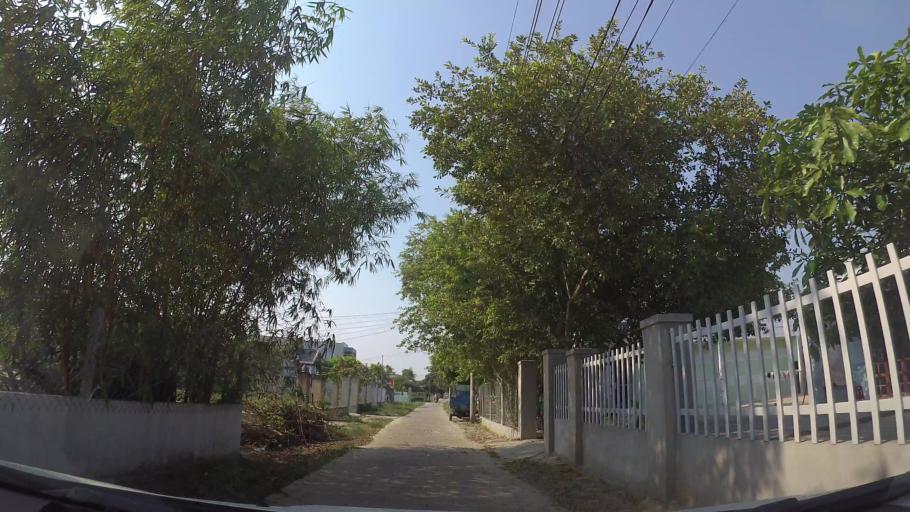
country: VN
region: Da Nang
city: Ngu Hanh Son
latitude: 15.9540
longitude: 108.2657
